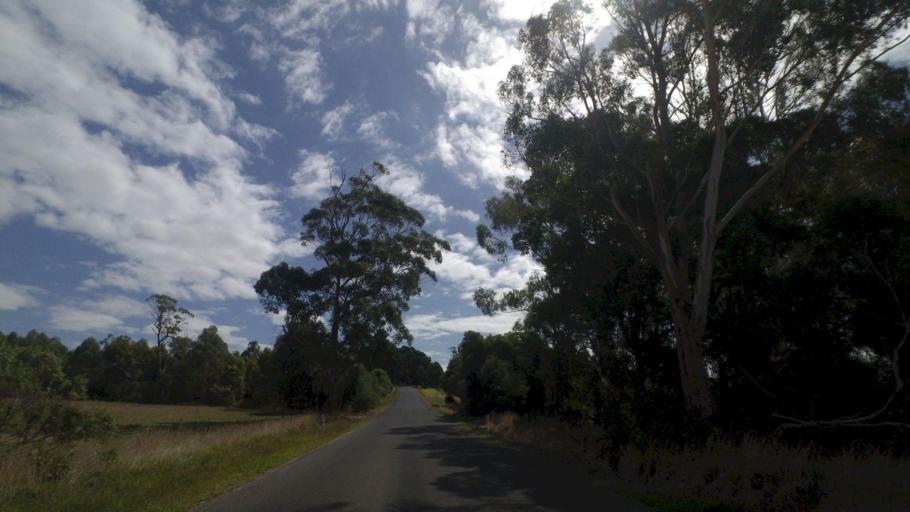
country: AU
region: Victoria
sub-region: Cardinia
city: Bunyip
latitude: -38.3082
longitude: 145.7657
